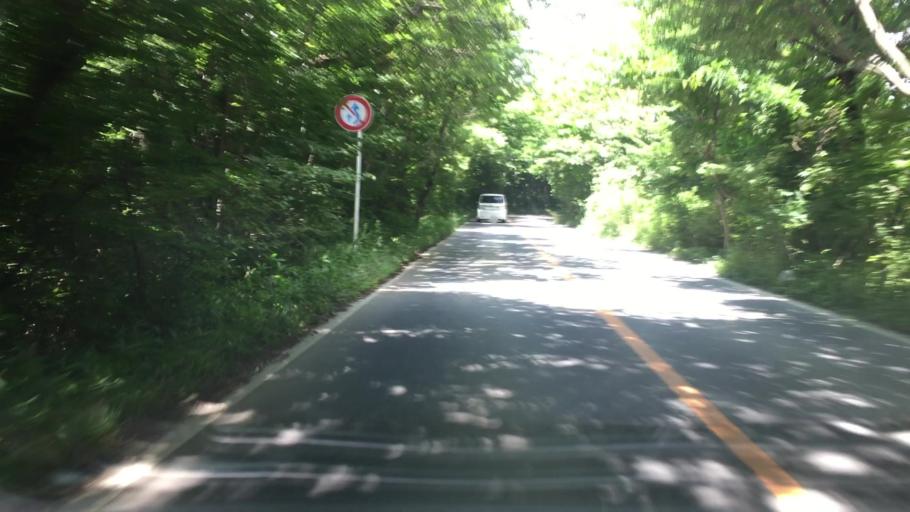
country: JP
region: Tochigi
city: Kuroiso
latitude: 37.0215
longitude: 140.0082
